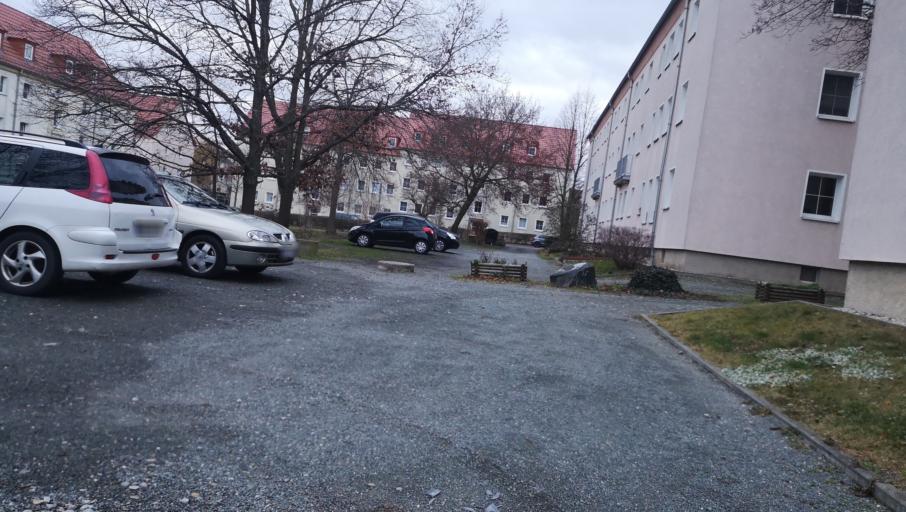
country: DE
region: Thuringia
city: Ronneburg
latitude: 50.8662
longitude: 12.1905
